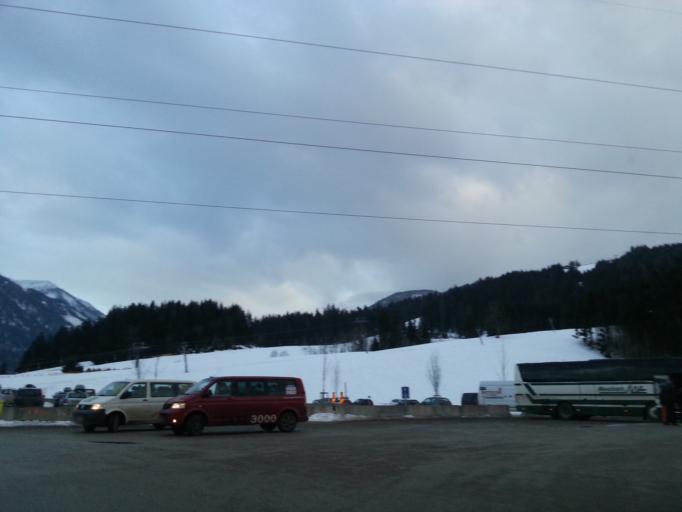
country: AT
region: Salzburg
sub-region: Politischer Bezirk Sankt Johann im Pongau
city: Flachau
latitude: 47.3604
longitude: 13.3812
